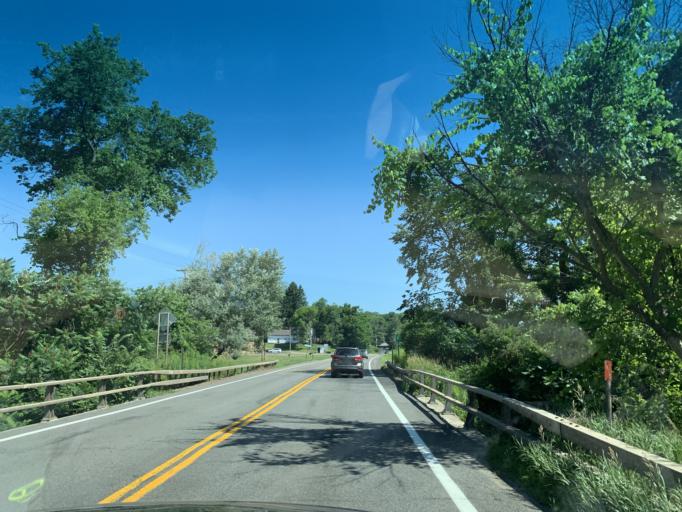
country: US
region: New York
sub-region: Delaware County
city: Sidney
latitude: 42.3328
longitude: -75.4087
